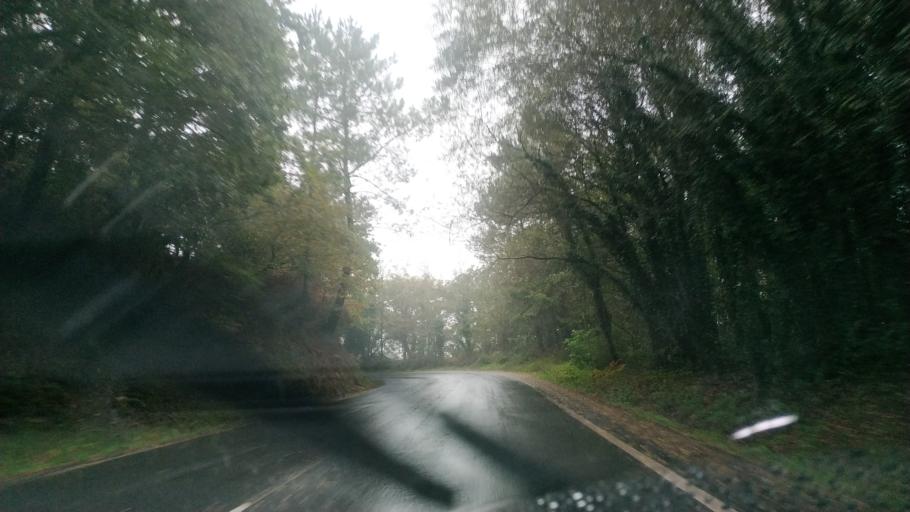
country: ES
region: Galicia
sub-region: Provincia da Coruna
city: Negreira
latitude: 42.9082
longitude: -8.7479
